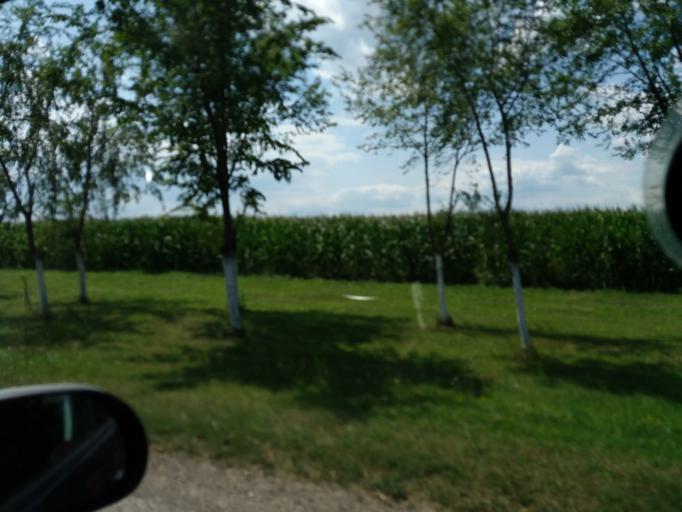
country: RS
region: Autonomna Pokrajina Vojvodina
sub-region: Sremski Okrug
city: Pecinci
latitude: 44.8603
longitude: 19.9601
